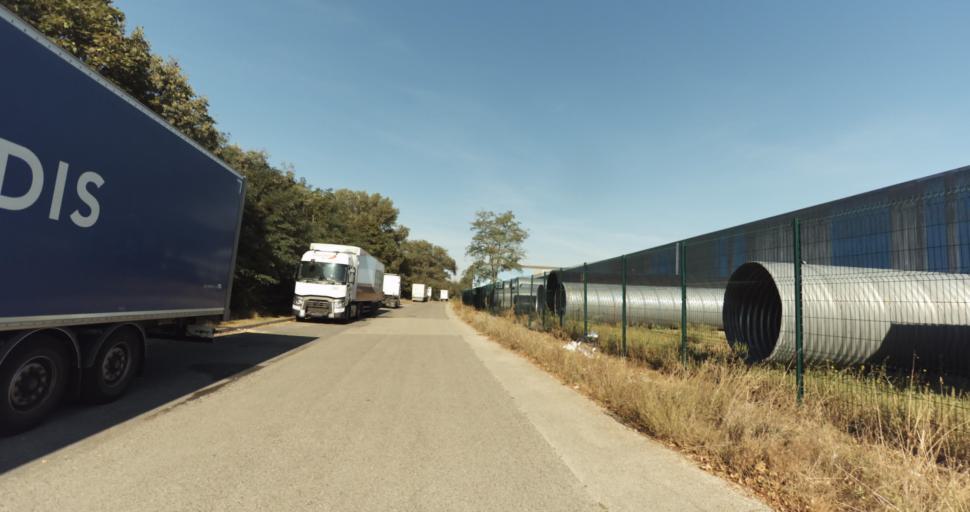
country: FR
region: Rhone-Alpes
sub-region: Departement du Rhone
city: Albigny-sur-Saone
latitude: 45.8827
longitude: 4.8209
